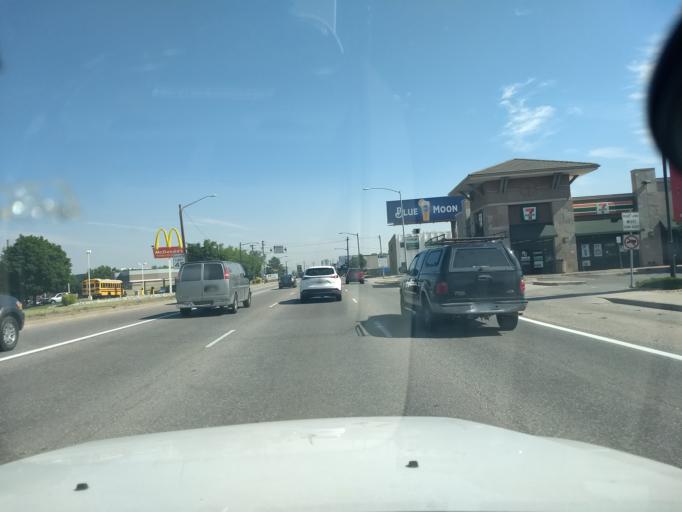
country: US
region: Colorado
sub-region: Arapahoe County
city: Englewood
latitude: 39.6899
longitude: -104.9922
